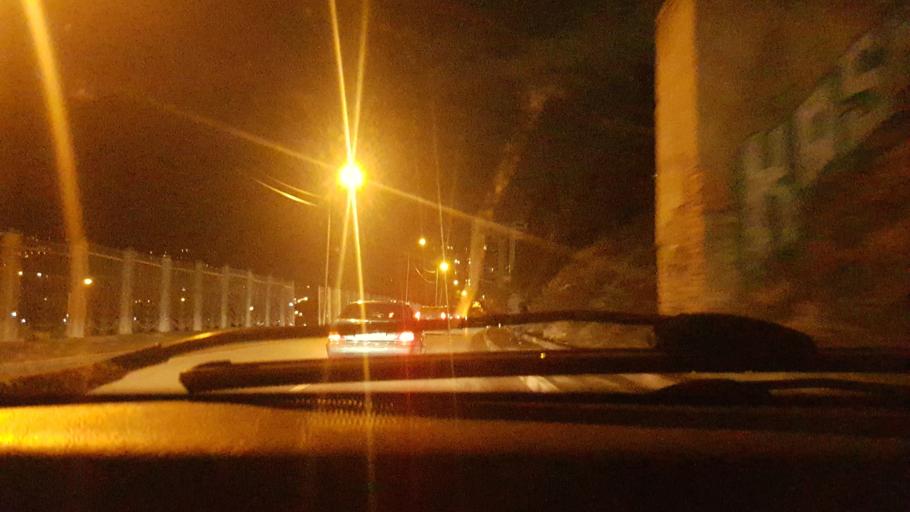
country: GE
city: Tsqnet'i
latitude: 41.7214
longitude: 44.7565
